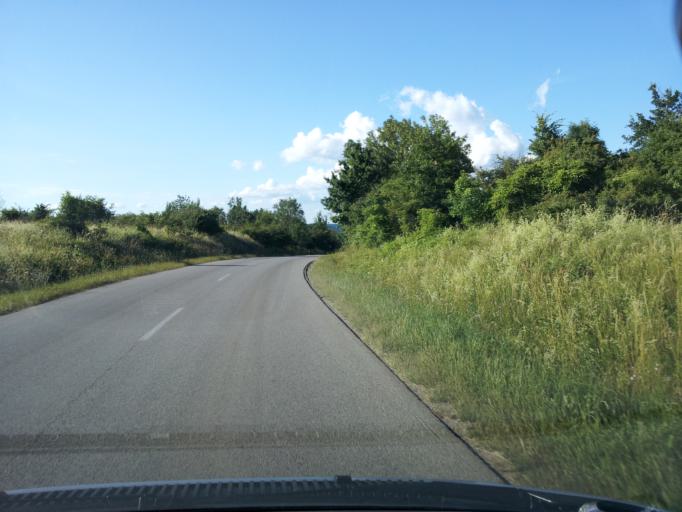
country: HU
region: Veszprem
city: Zirc
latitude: 47.2430
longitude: 17.8578
